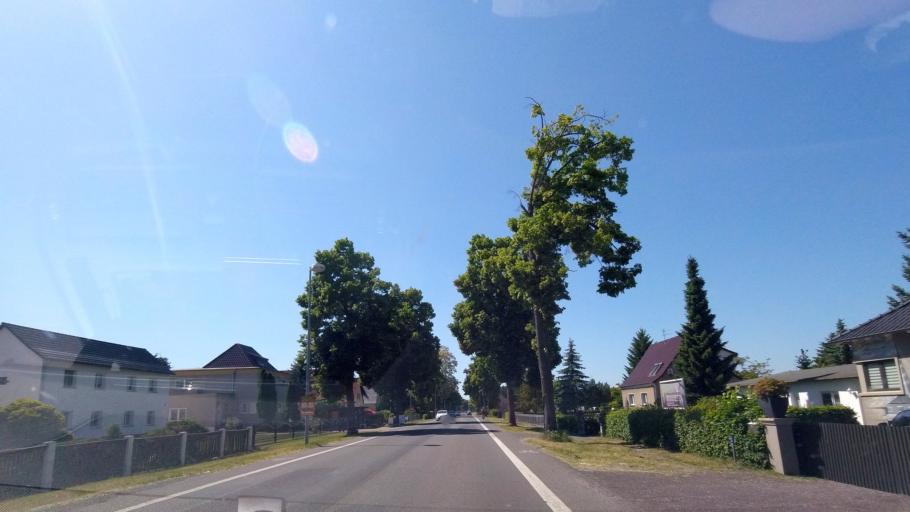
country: DE
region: Brandenburg
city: Gross Kreutz
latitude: 52.4070
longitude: 12.7381
